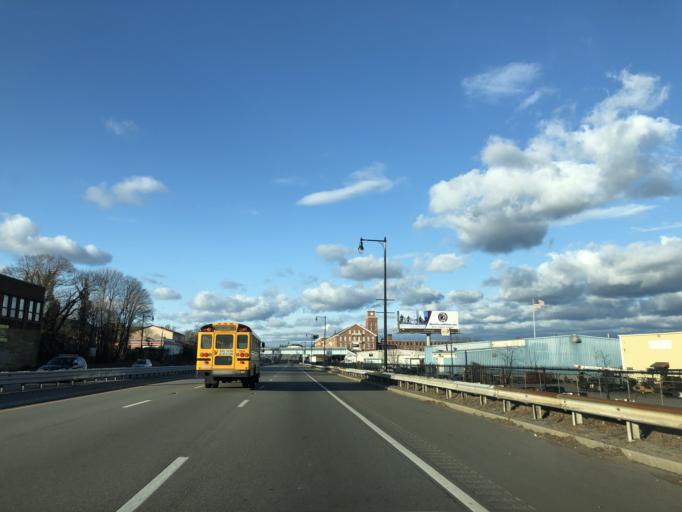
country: US
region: Massachusetts
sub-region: Bristol County
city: New Bedford
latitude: 41.6456
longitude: -70.9269
